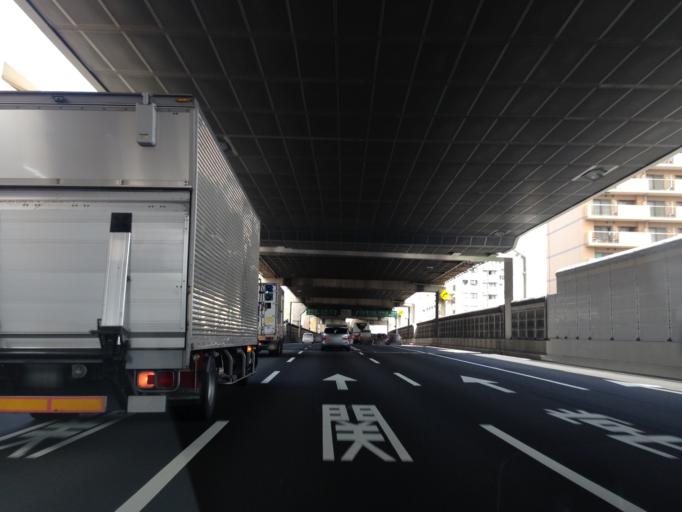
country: JP
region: Saitama
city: Kawaguchi
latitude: 35.7471
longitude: 139.7083
